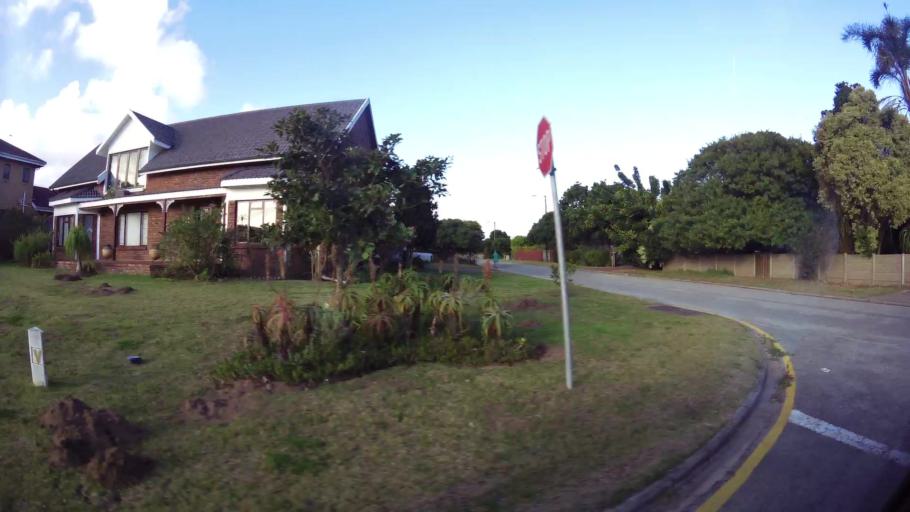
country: ZA
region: Western Cape
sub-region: Eden District Municipality
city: George
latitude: -33.9957
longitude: 22.6115
